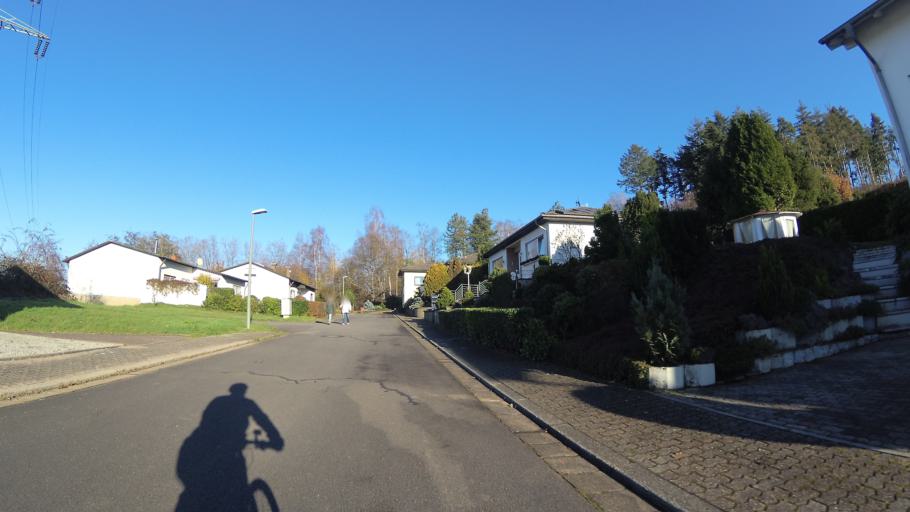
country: DE
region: Saarland
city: Schwalbach
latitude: 49.2992
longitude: 6.8286
